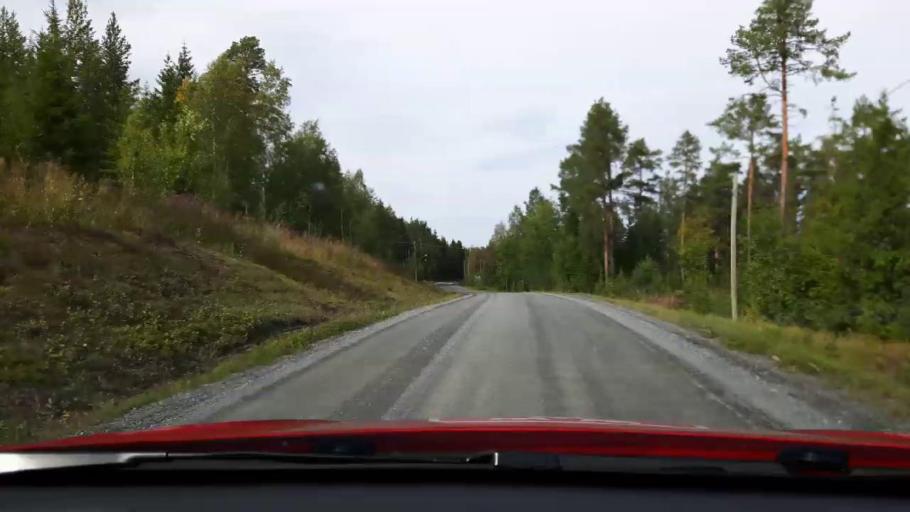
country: SE
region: Jaemtland
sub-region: Krokoms Kommun
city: Valla
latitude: 63.2656
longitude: 13.9116
